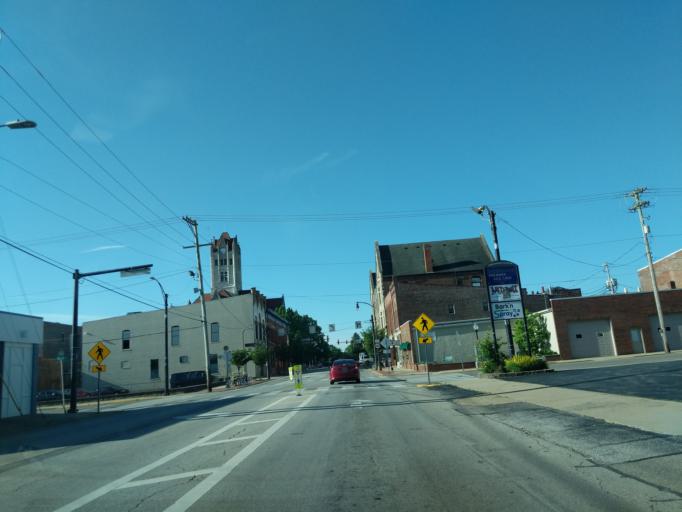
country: US
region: Indiana
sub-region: Hancock County
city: Greenfield
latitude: 39.7866
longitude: -85.7695
